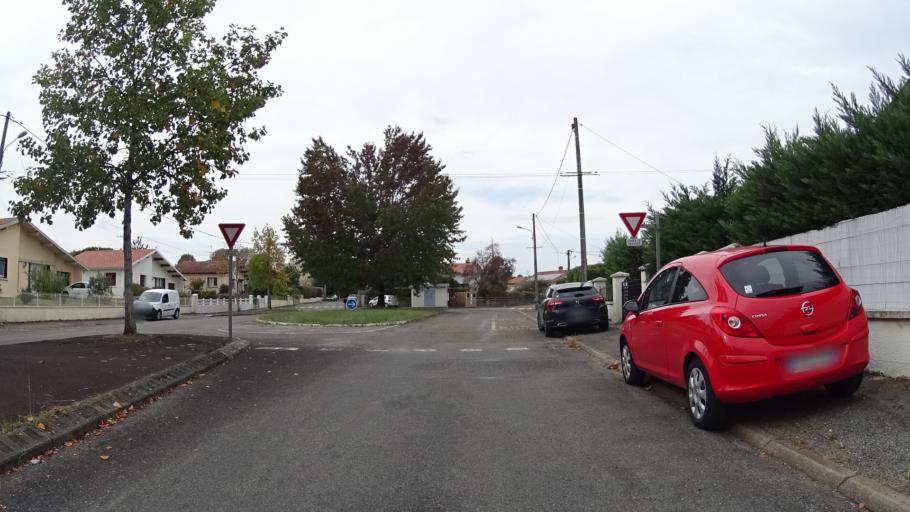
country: FR
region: Aquitaine
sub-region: Departement des Landes
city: Saint-Paul-les-Dax
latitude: 43.7278
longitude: -1.0717
